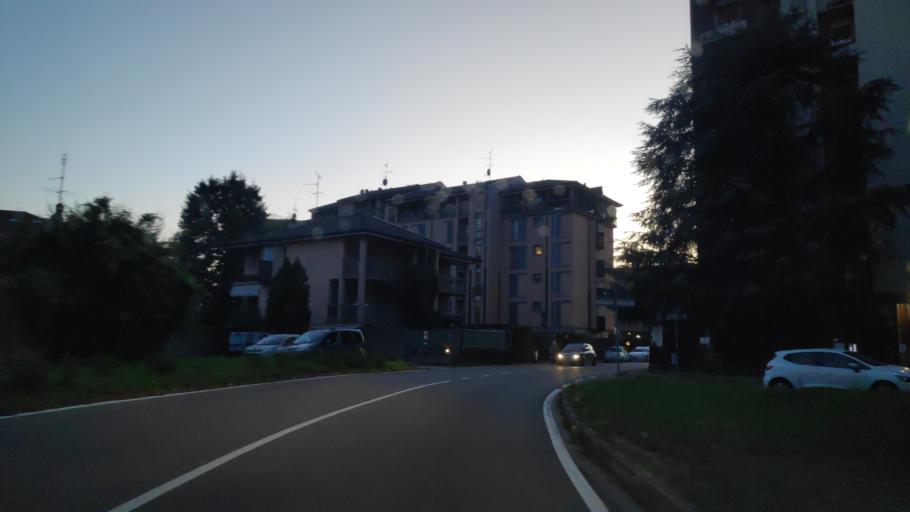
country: IT
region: Lombardy
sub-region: Citta metropolitana di Milano
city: Abbiategrasso
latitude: 45.4015
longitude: 8.9213
